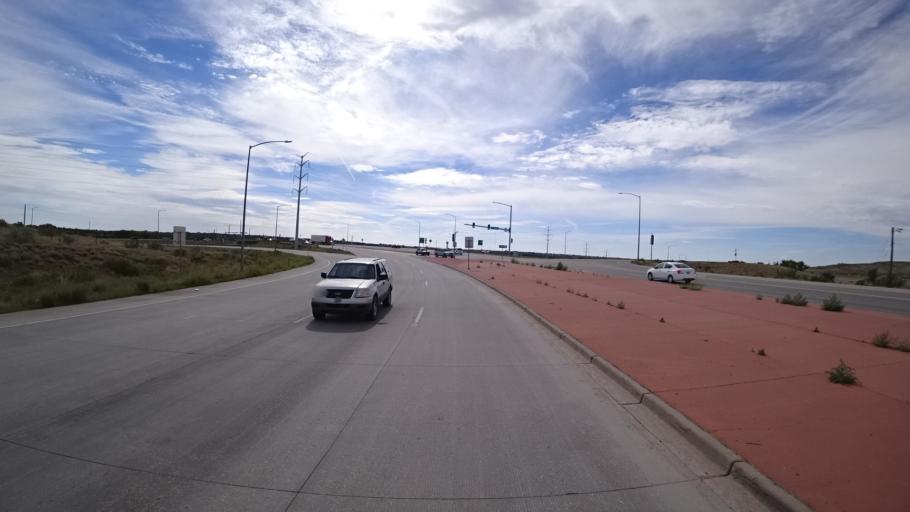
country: US
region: Colorado
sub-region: El Paso County
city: Security-Widefield
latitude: 38.7245
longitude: -104.7357
